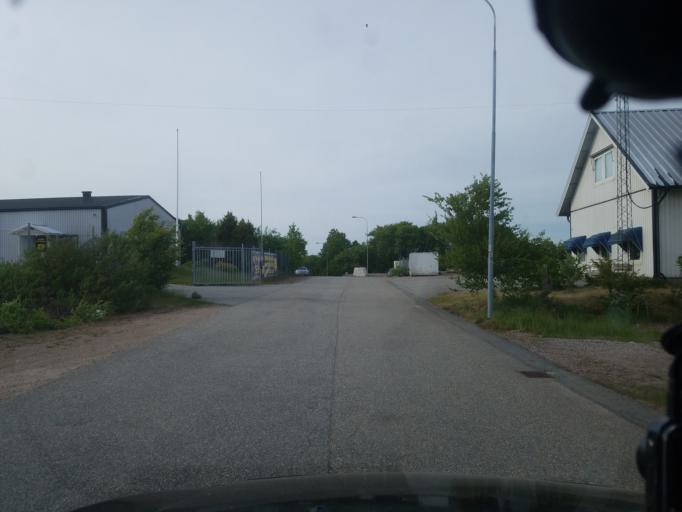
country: SE
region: Vaestra Goetaland
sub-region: Lysekils Kommun
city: Lysekil
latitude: 58.2880
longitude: 11.4569
